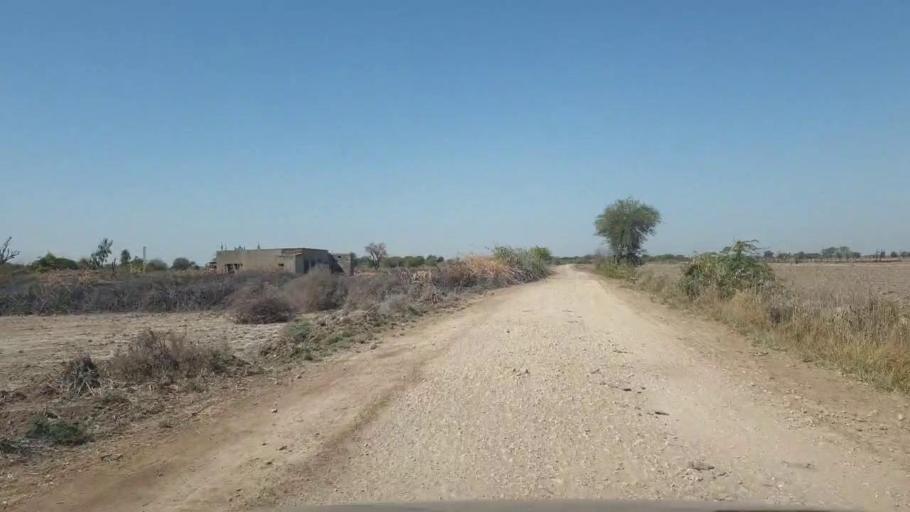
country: PK
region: Sindh
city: Dhoro Naro
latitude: 25.4493
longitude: 69.6137
